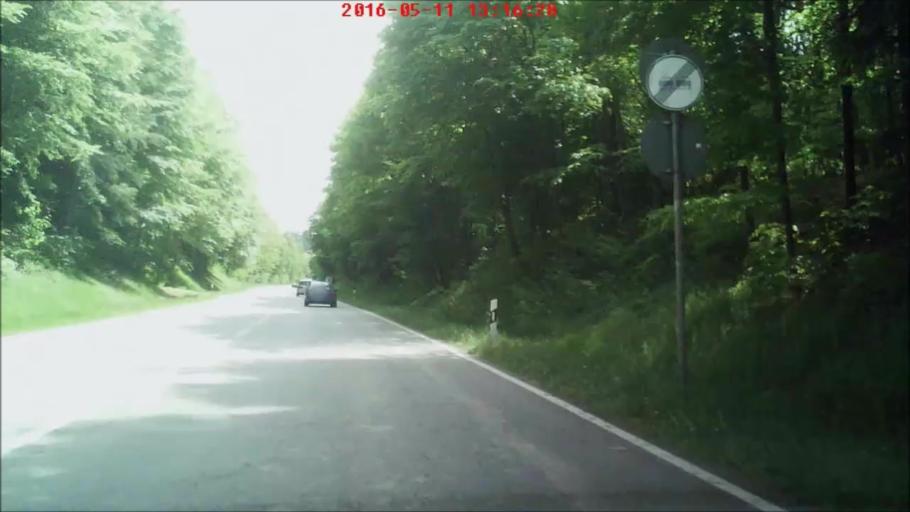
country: DE
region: Bavaria
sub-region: Lower Bavaria
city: Passau
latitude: 48.5493
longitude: 13.4059
